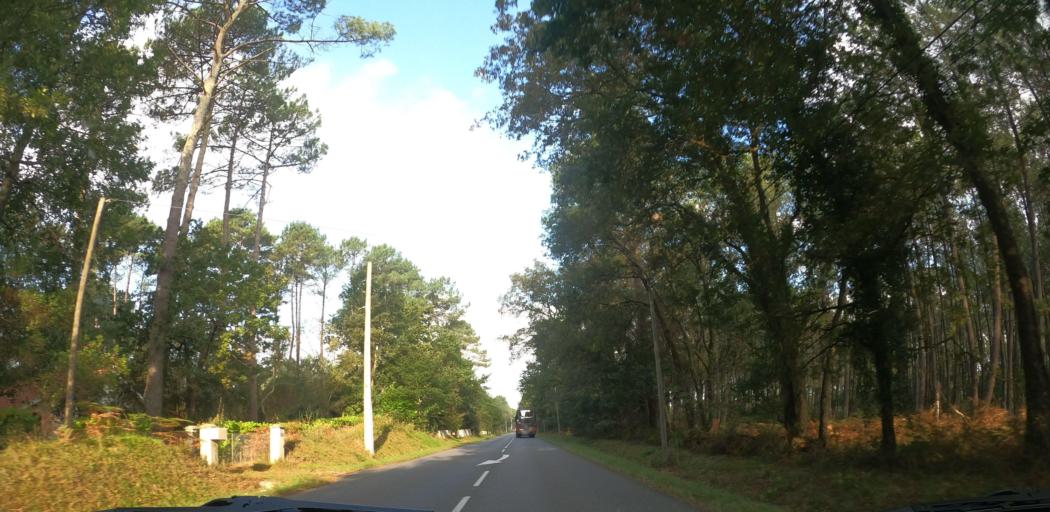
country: FR
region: Aquitaine
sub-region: Departement des Landes
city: Soustons
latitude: 43.7346
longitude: -1.2908
